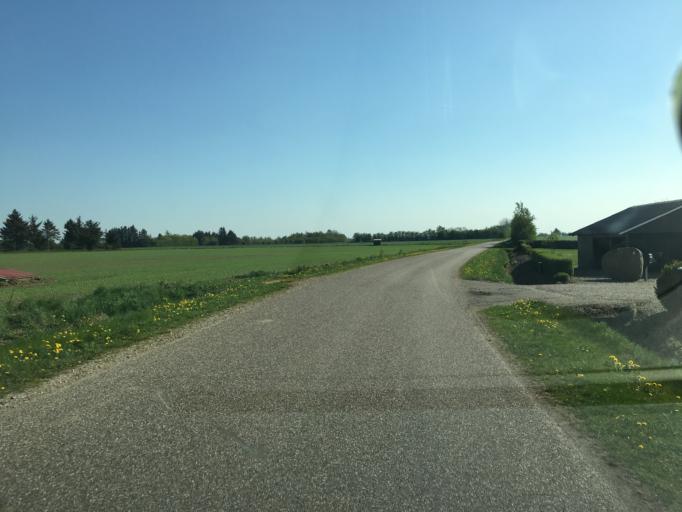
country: DK
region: South Denmark
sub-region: Tonder Kommune
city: Toftlund
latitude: 55.1859
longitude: 9.1106
